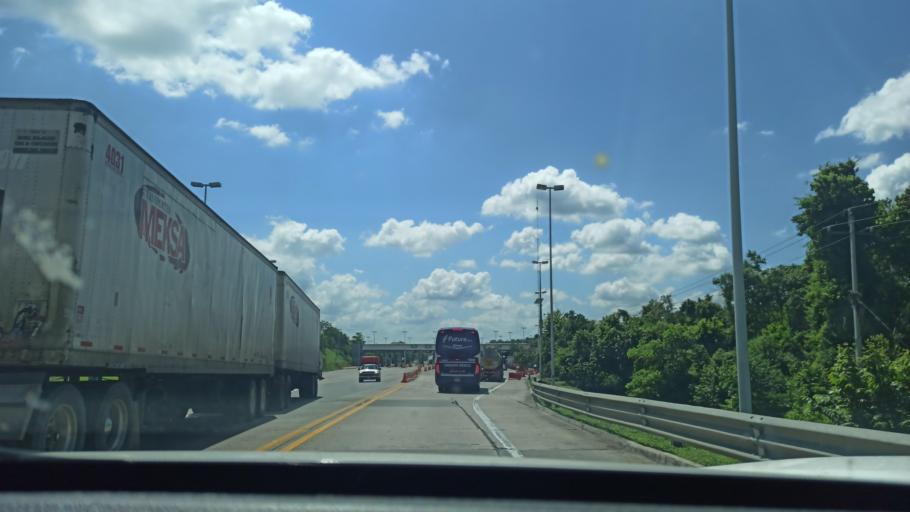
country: MX
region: Veracruz
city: Tihuatlan
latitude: 20.7556
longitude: -97.4823
